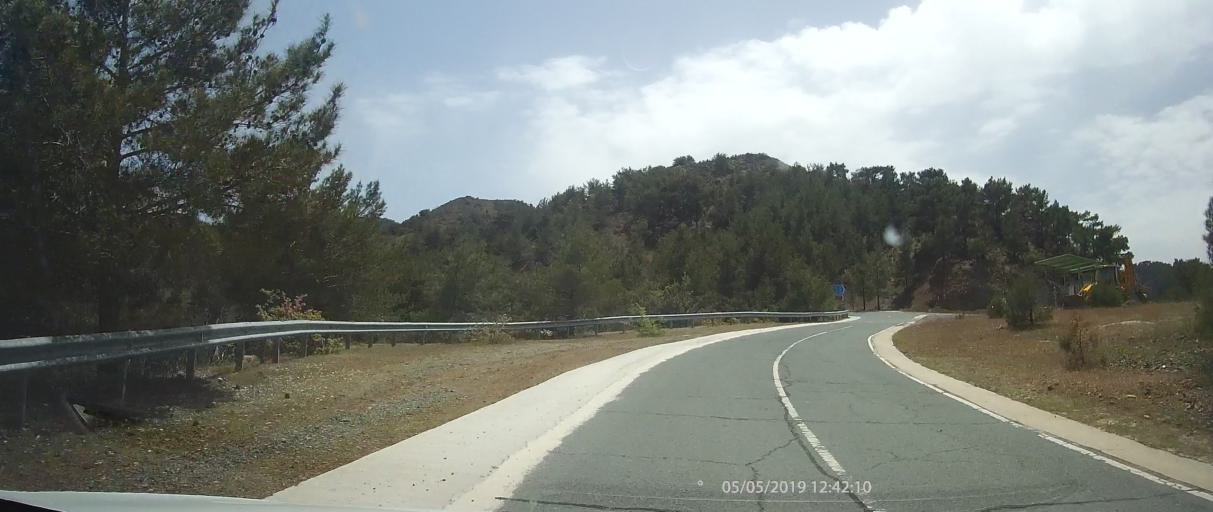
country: CY
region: Lefkosia
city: Kakopetria
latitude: 34.9761
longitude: 32.8096
